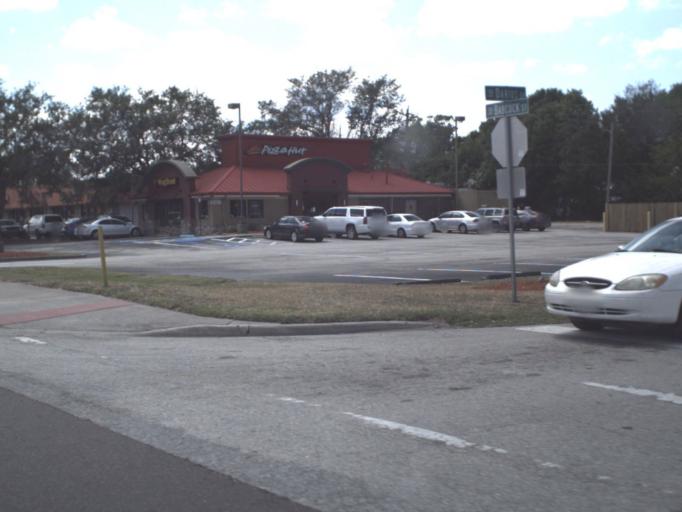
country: US
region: Florida
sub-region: Brevard County
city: Palm Bay
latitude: 28.0303
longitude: -80.6220
